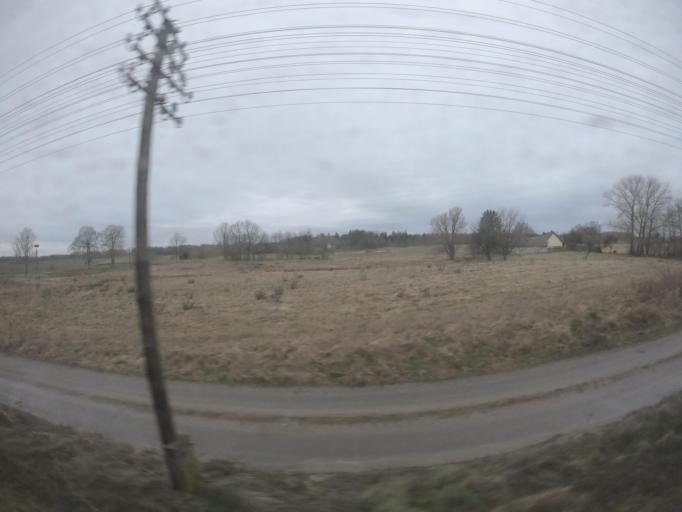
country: PL
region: West Pomeranian Voivodeship
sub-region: Powiat szczecinecki
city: Szczecinek
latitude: 53.6600
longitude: 16.6281
